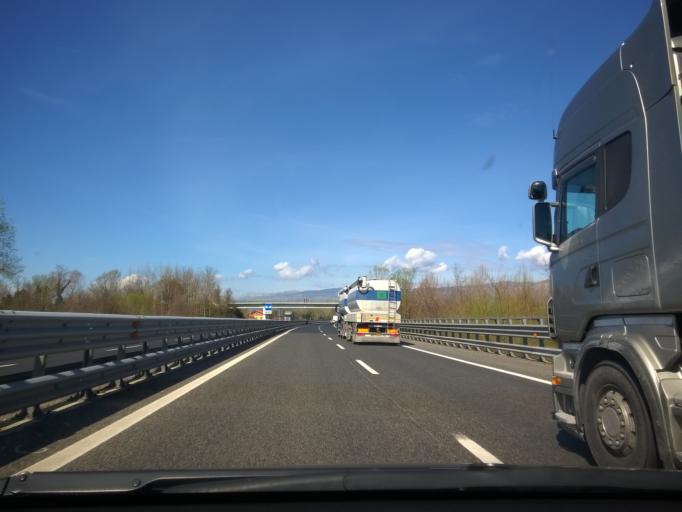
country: IT
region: Friuli Venezia Giulia
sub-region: Provincia di Pordenone
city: Azzano Decimo
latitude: 45.9304
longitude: 12.6757
